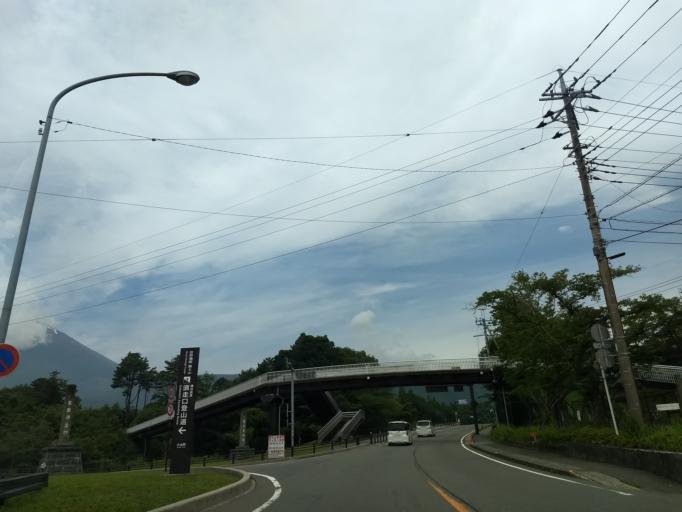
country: JP
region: Shizuoka
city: Gotemba
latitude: 35.3621
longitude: 138.8624
